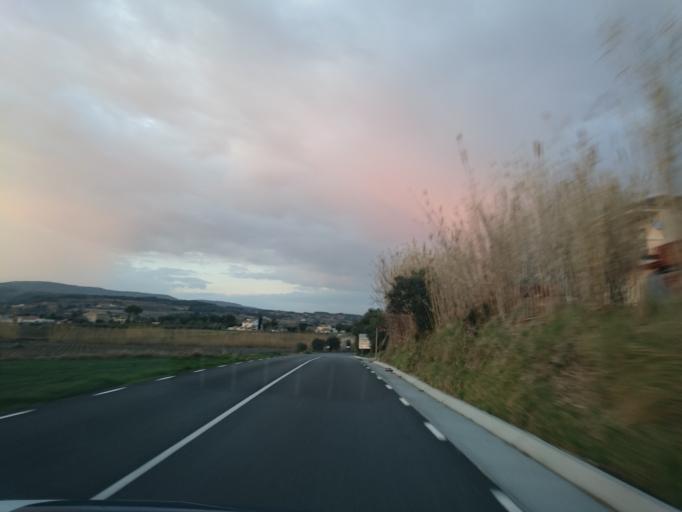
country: ES
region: Catalonia
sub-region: Provincia de Barcelona
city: Sant Marti Sarroca
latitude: 41.3887
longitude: 1.5971
